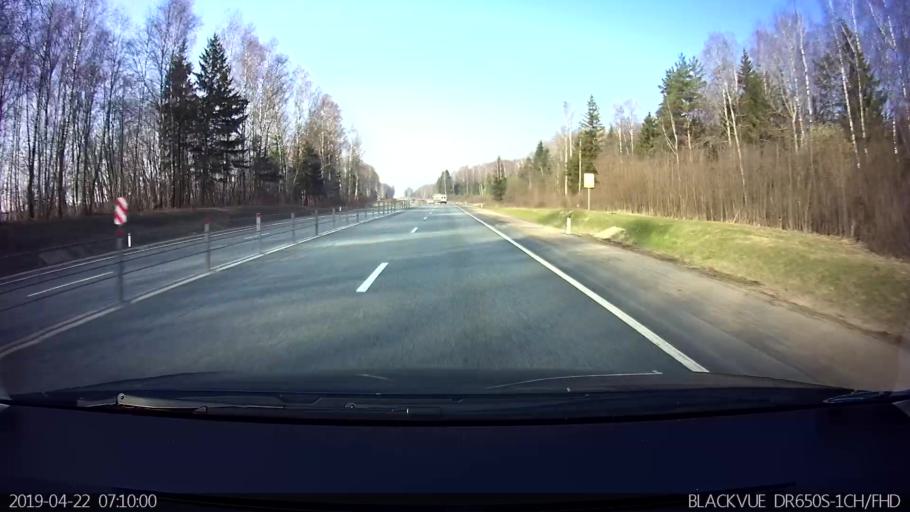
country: RU
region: Smolensk
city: Vyaz'ma
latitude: 55.3166
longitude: 34.5355
